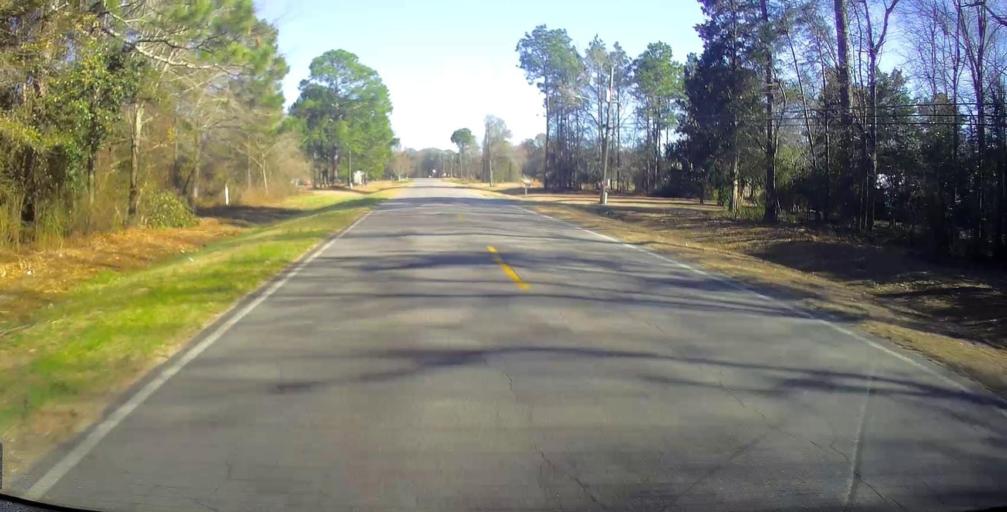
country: US
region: Georgia
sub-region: Taylor County
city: Butler
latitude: 32.5604
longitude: -84.2488
